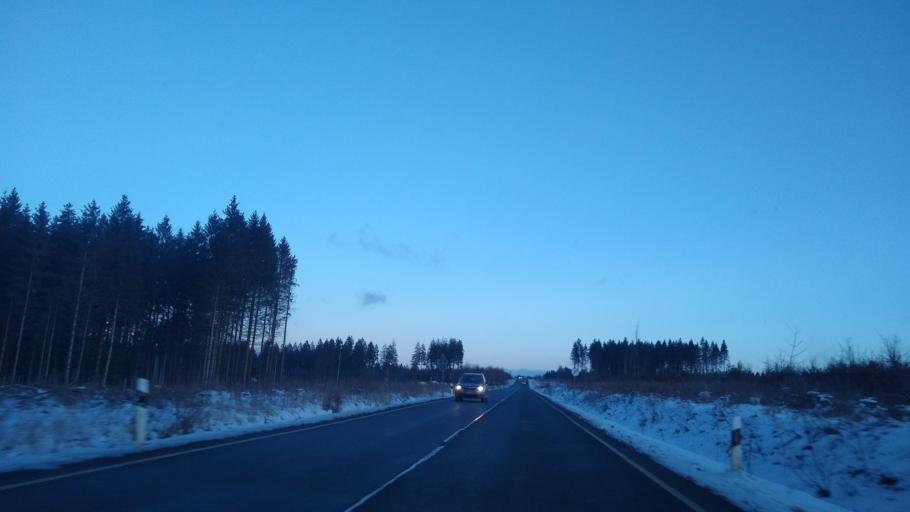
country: DE
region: Lower Saxony
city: Clausthal-Zellerfeld
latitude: 51.7902
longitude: 10.3696
